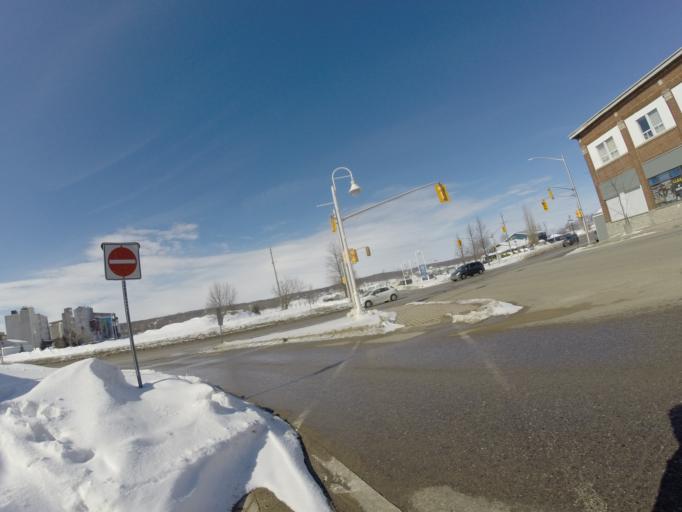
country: CA
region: Ontario
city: Midland
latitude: 44.7518
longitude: -79.8874
